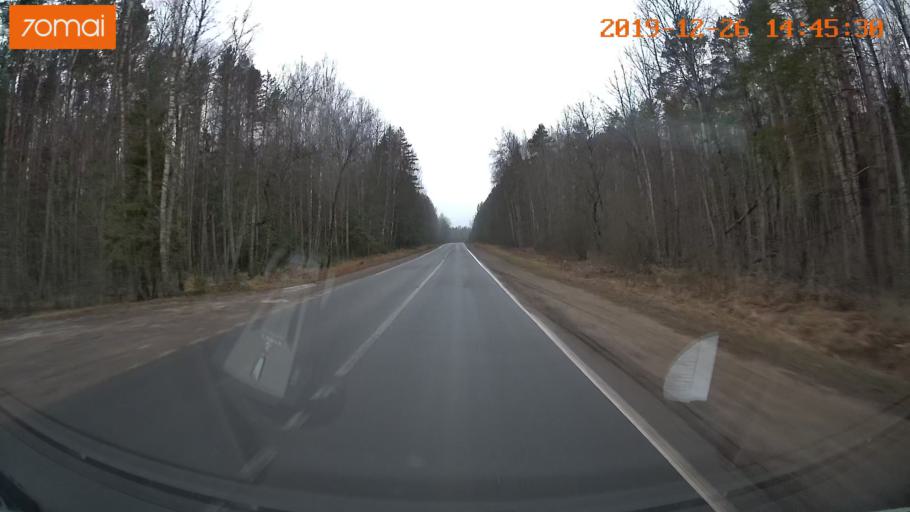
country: RU
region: Jaroslavl
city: Poshekhon'ye
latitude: 58.3378
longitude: 39.0383
